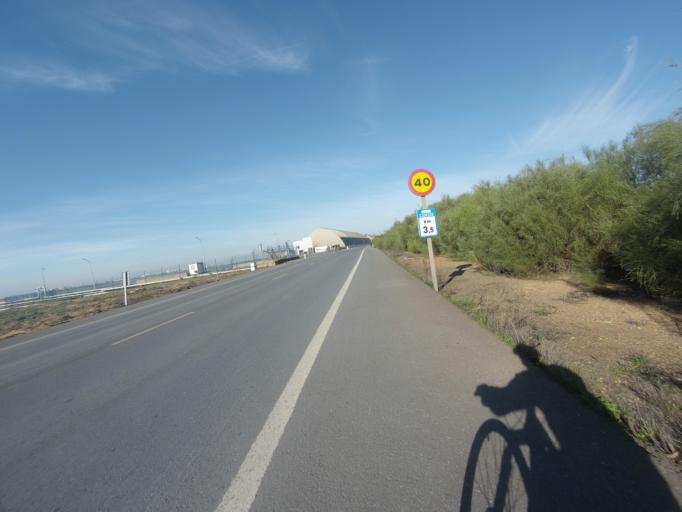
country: ES
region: Andalusia
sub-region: Provincia de Huelva
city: Punta Umbria
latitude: 37.1782
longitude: -6.9180
